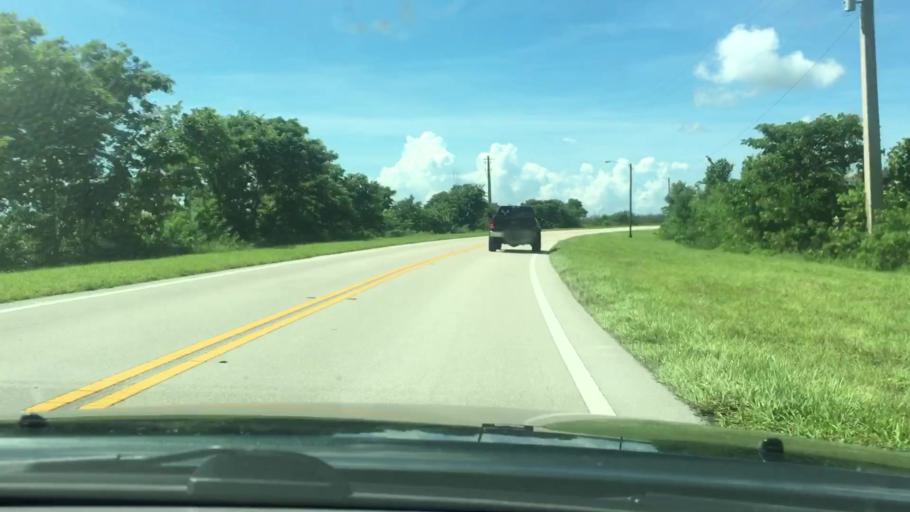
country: US
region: Florida
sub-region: Collier County
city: Marco
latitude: 25.9352
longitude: -81.6483
